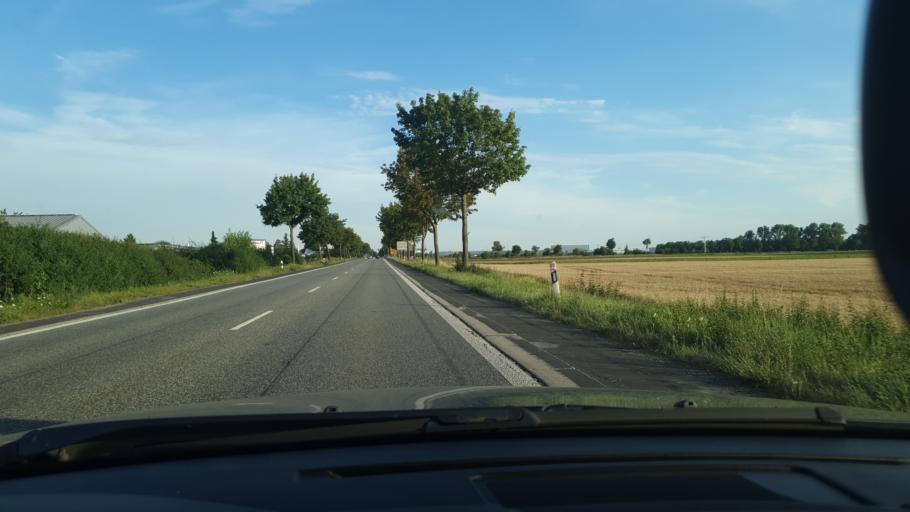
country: DE
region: Rheinland-Pfalz
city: Osthofen
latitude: 49.7101
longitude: 8.3487
